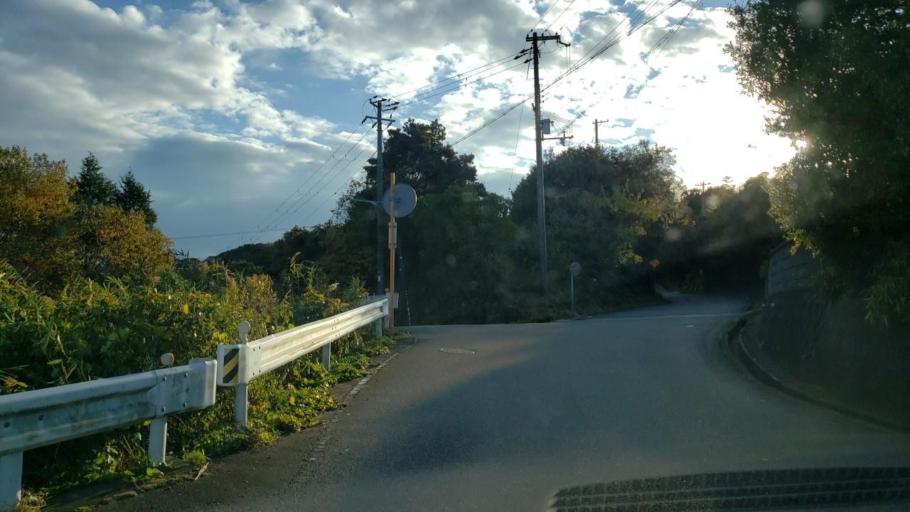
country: JP
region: Hyogo
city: Akashi
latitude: 34.5418
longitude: 134.9640
